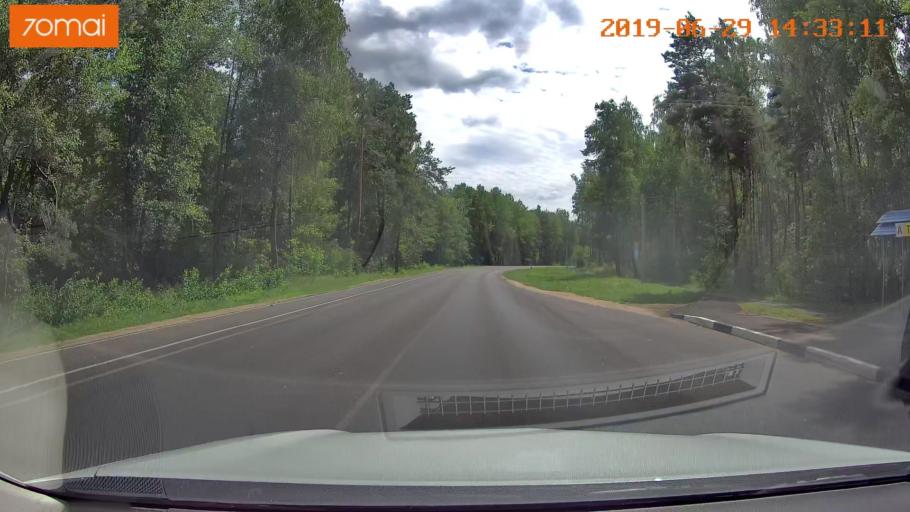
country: BY
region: Minsk
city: Salihorsk
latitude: 52.7801
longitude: 27.5019
